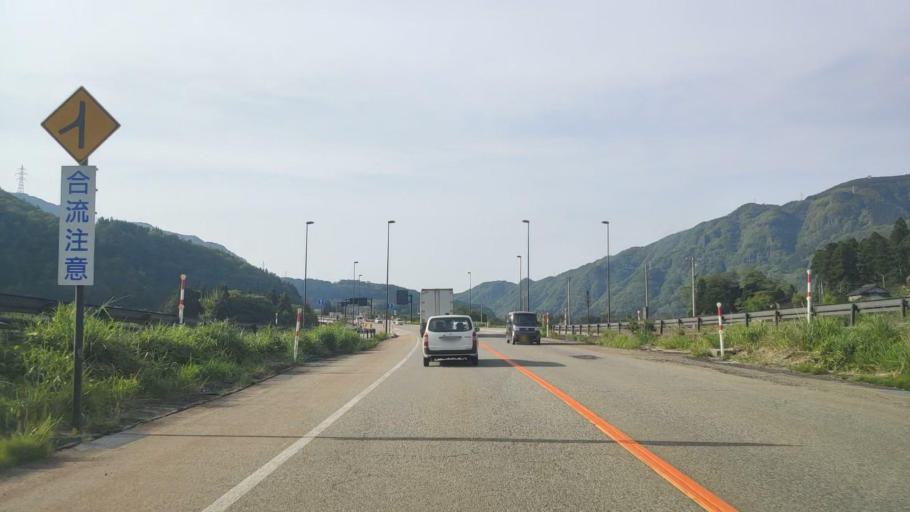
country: JP
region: Toyama
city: Yatsuomachi-higashikumisaka
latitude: 36.5231
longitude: 137.2310
